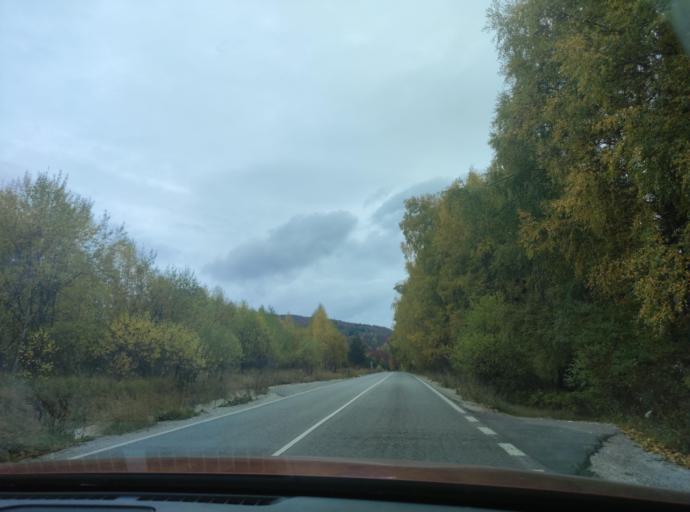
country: BG
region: Sofiya
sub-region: Obshtina Godech
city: Godech
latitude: 43.1008
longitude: 23.1017
